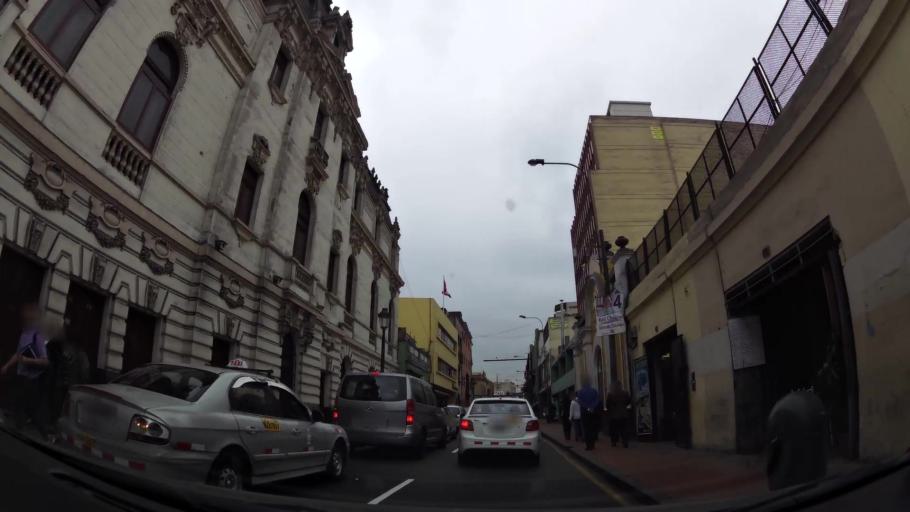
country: PE
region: Lima
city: Lima
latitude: -12.0550
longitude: -77.0357
